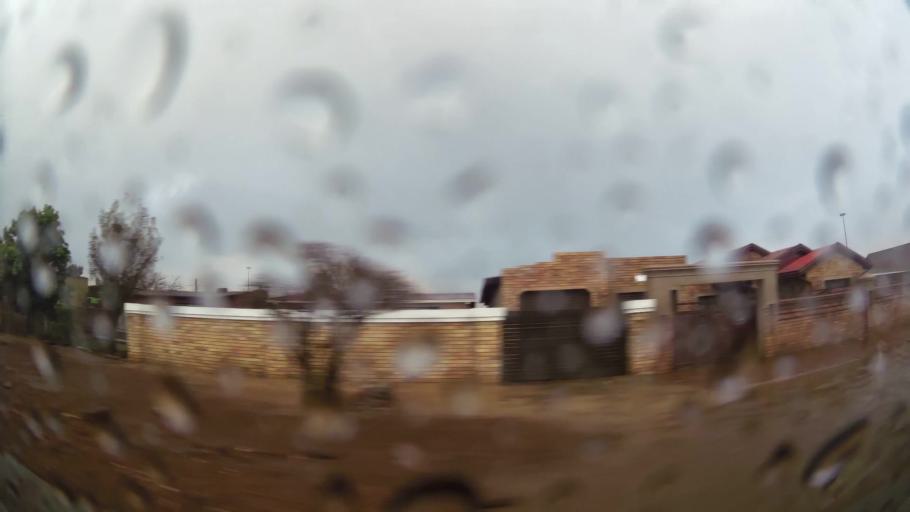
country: ZA
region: Gauteng
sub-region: Ekurhuleni Metropolitan Municipality
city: Germiston
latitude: -26.3528
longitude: 28.1411
